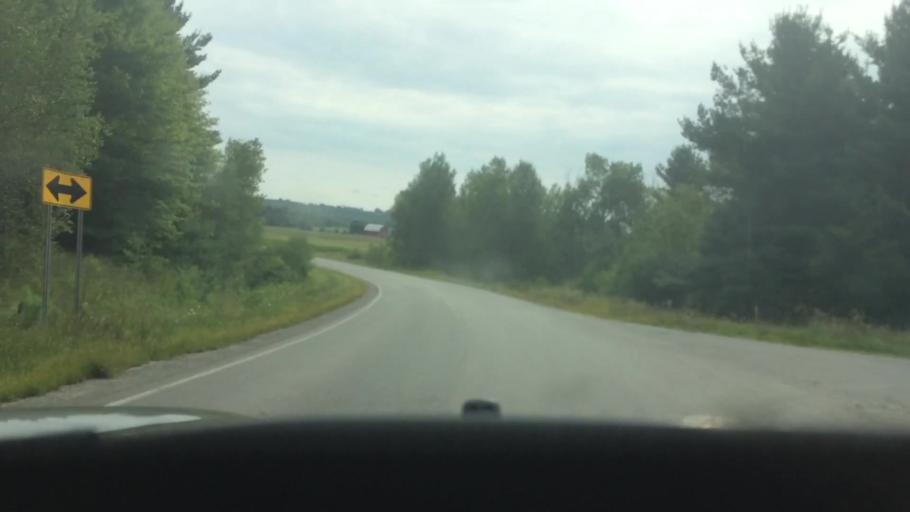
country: US
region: New York
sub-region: St. Lawrence County
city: Canton
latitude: 44.4957
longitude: -75.2612
